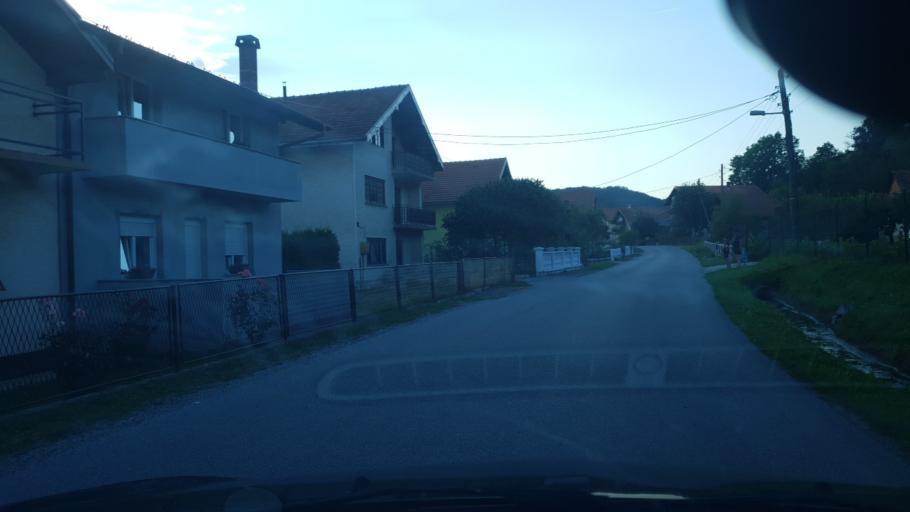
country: HR
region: Krapinsko-Zagorska
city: Zabok
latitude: 46.0395
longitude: 15.8906
